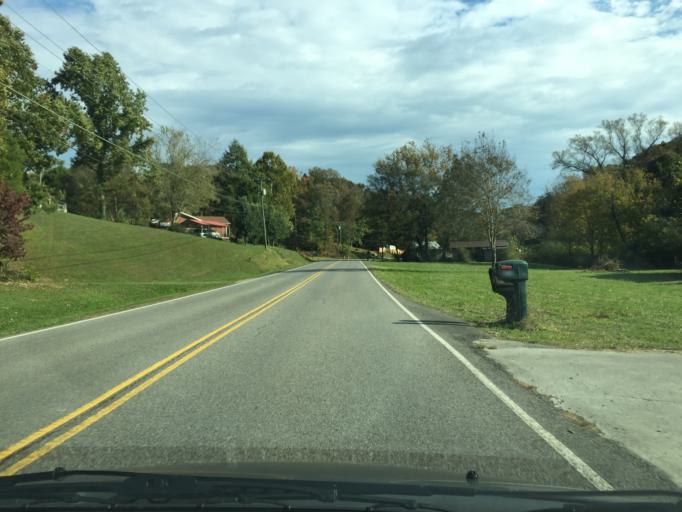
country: US
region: Tennessee
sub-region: Loudon County
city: Loudon
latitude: 35.6983
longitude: -84.3382
